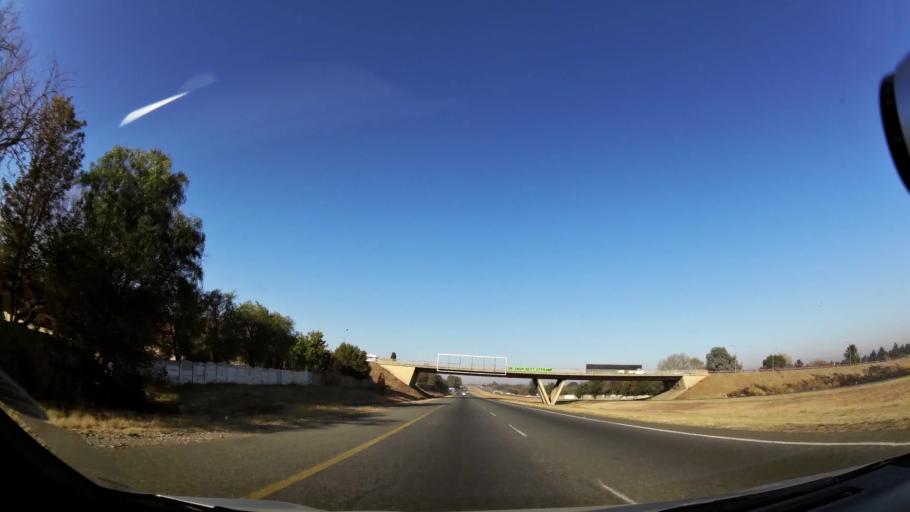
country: ZA
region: Gauteng
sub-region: Ekurhuleni Metropolitan Municipality
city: Germiston
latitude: -26.3377
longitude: 28.1074
